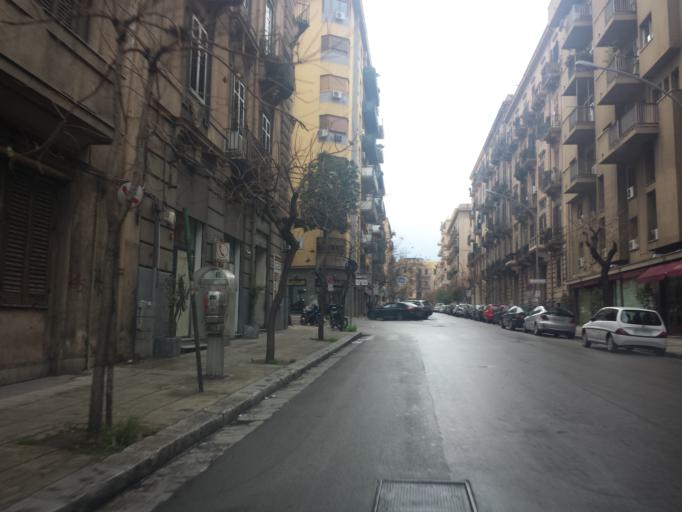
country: IT
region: Sicily
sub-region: Palermo
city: Palermo
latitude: 38.1222
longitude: 13.3509
